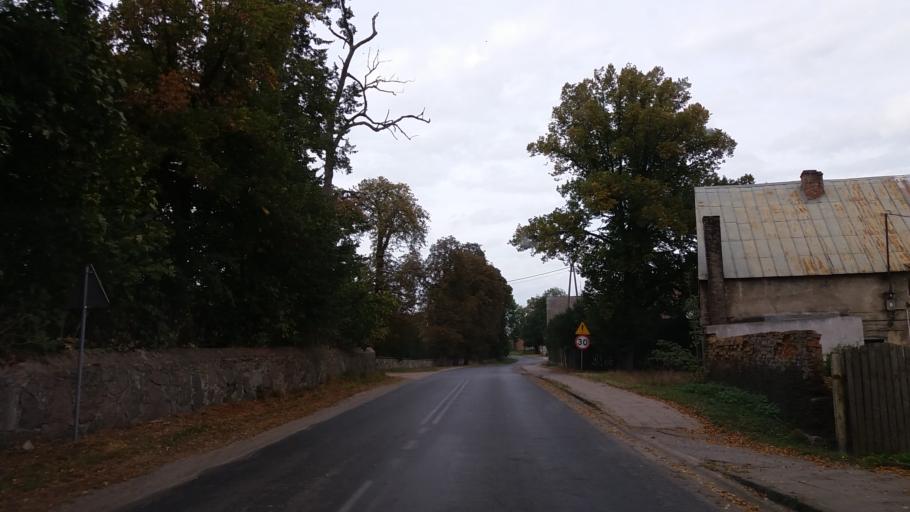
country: PL
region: Lubusz
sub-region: Powiat strzelecko-drezdenecki
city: Strzelce Krajenskie
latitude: 52.9075
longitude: 15.5020
